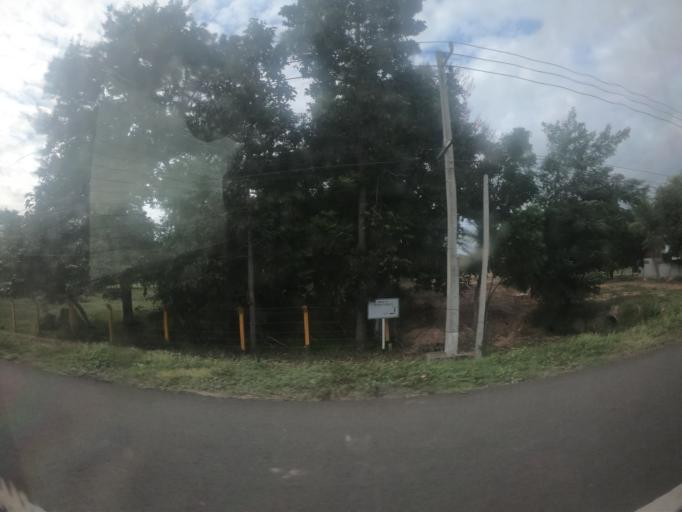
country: TH
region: Surin
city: Prasat
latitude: 14.5909
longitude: 103.4563
